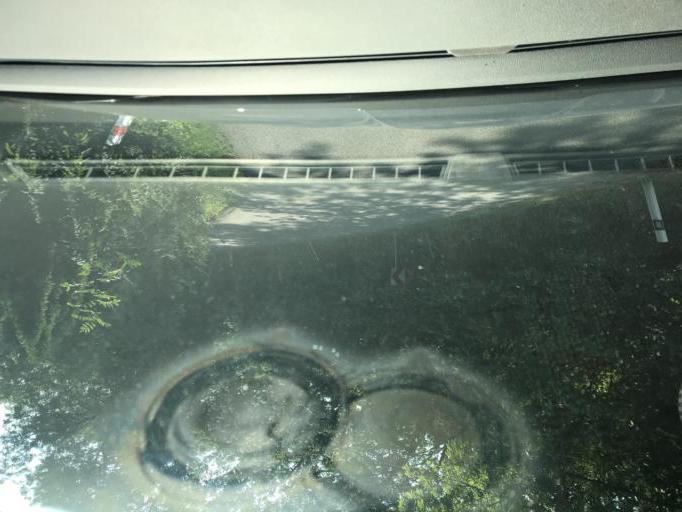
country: CZ
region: Central Bohemia
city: Kralupy nad Vltavou
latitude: 50.2177
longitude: 14.3278
